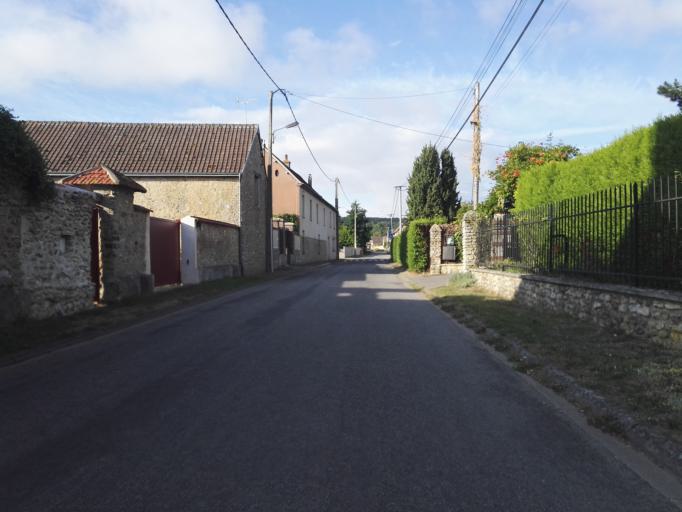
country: FR
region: Haute-Normandie
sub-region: Departement de l'Eure
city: Menilles
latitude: 49.0411
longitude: 1.3193
